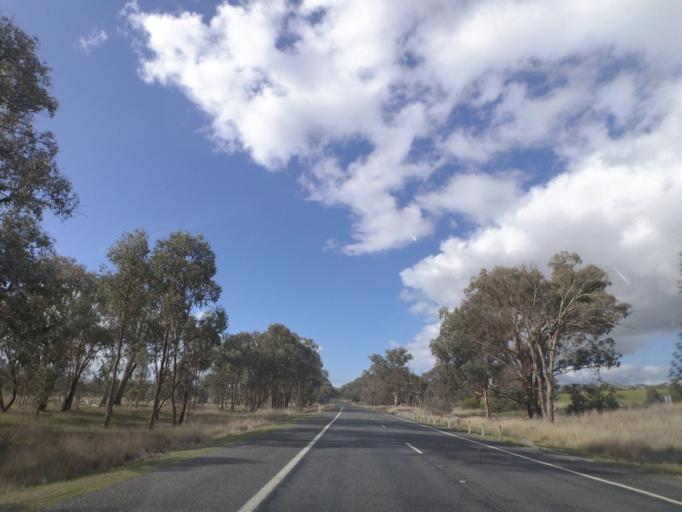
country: AU
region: New South Wales
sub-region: Greater Hume Shire
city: Holbrook
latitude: -35.6768
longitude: 147.3718
